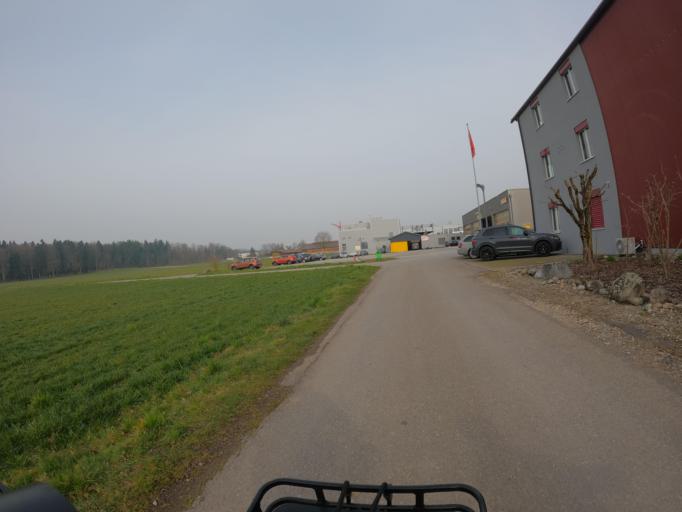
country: CH
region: Aargau
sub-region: Bezirk Bremgarten
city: Bremgarten
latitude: 47.3406
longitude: 8.3539
